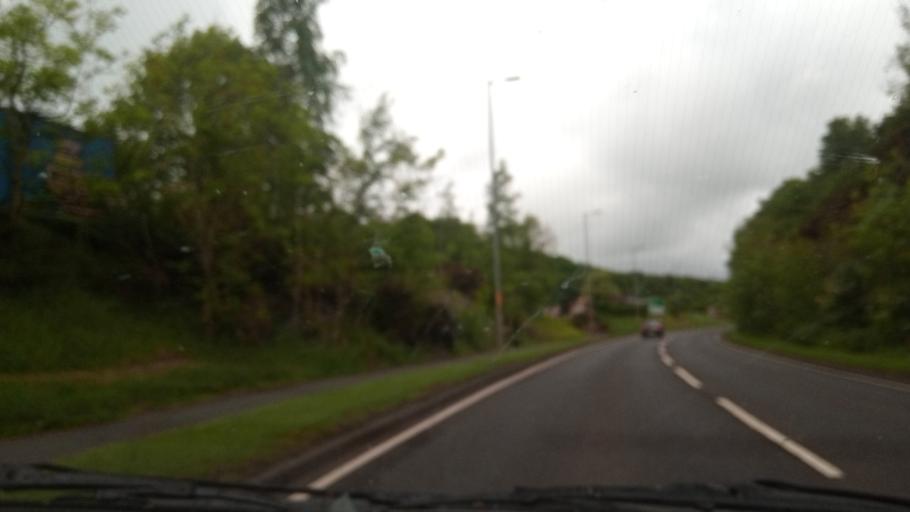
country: GB
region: Scotland
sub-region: The Scottish Borders
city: Hawick
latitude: 55.4357
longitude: -2.7800
